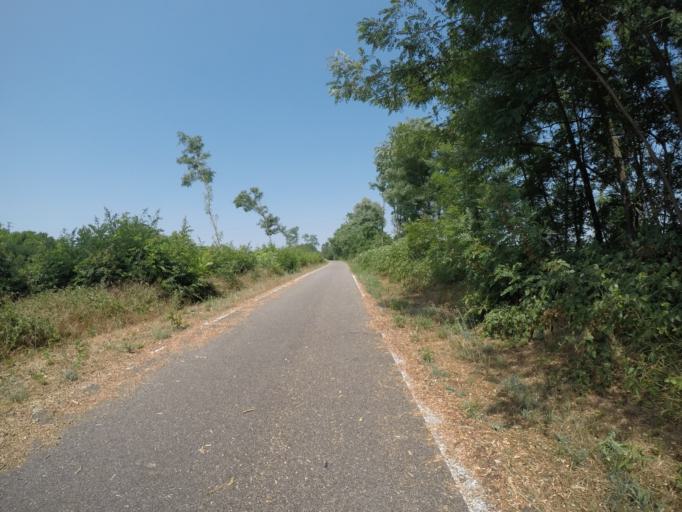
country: IT
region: Veneto
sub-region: Provincia di Rovigo
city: Villamarzana
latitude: 45.0085
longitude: 11.6750
